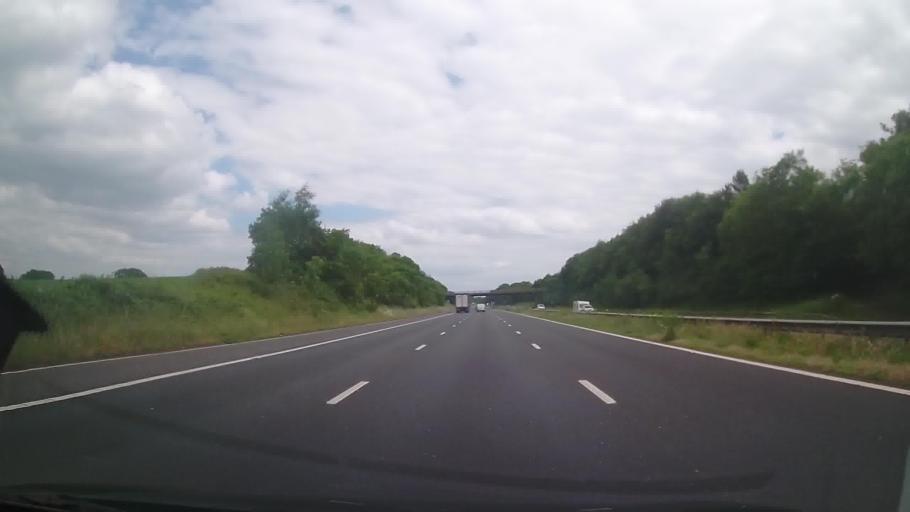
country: GB
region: England
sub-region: Devon
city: Uffculme
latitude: 50.9591
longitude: -3.2360
